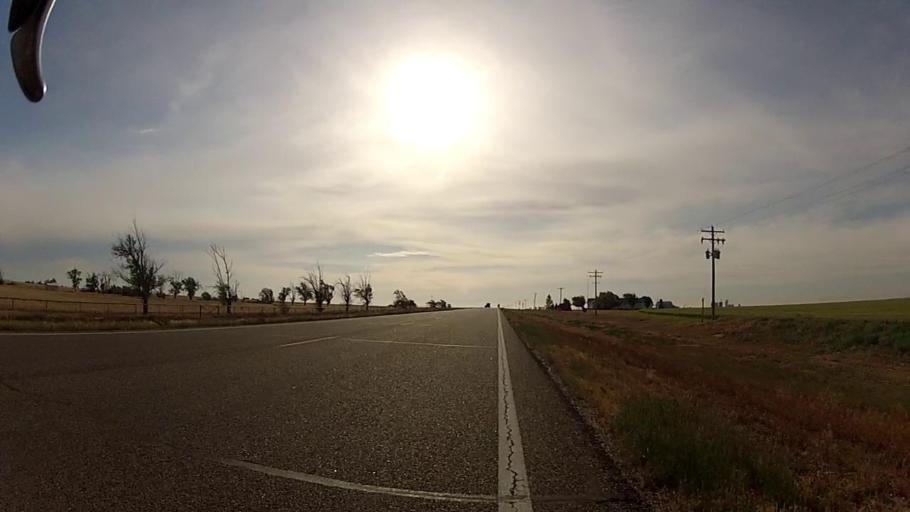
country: US
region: Kansas
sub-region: Grant County
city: Ulysses
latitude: 37.5766
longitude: -101.4859
